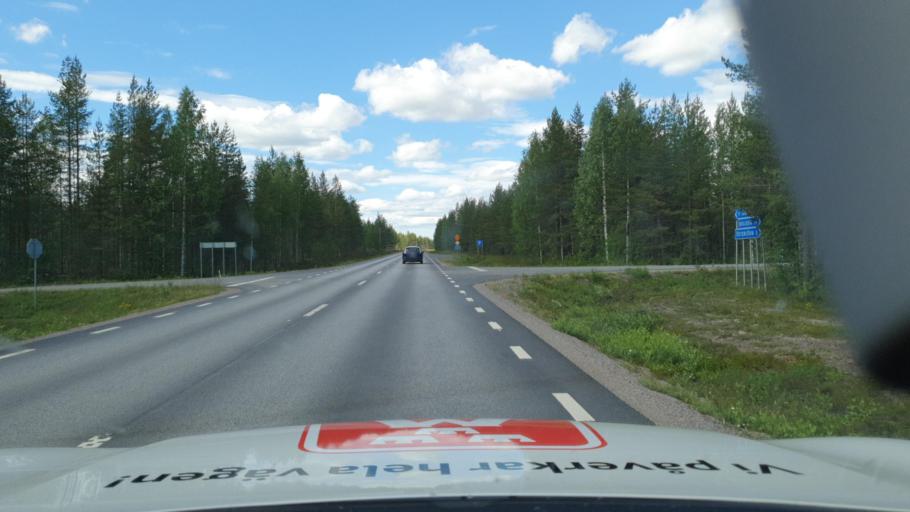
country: SE
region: Vaesterbotten
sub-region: Skelleftea Kommun
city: Langsele
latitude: 65.0065
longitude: 20.1788
